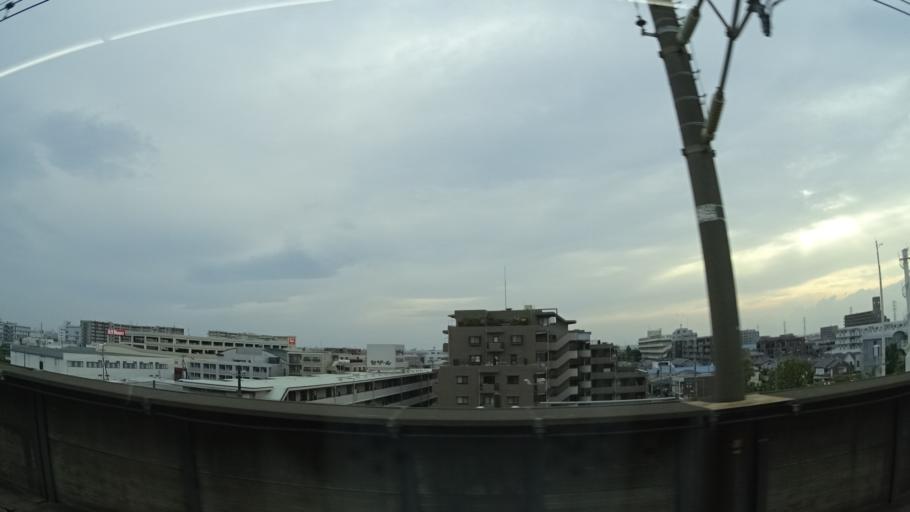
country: JP
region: Saitama
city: Shimotoda
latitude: 35.8361
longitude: 139.6519
